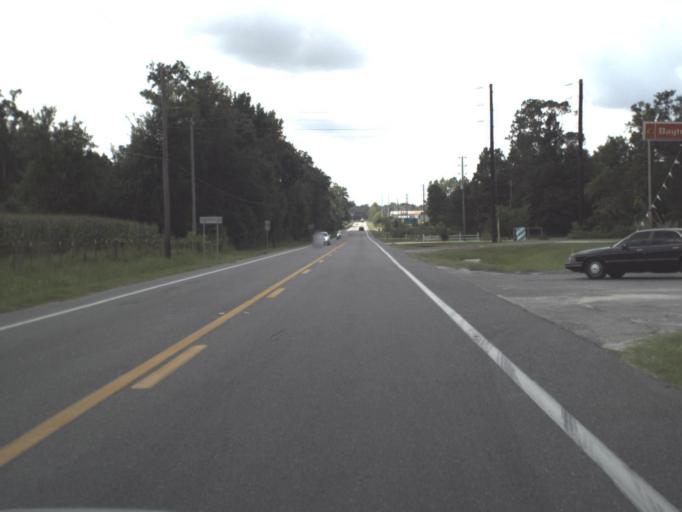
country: US
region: Florida
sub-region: Union County
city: Lake Butler
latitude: 29.9458
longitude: -82.4248
